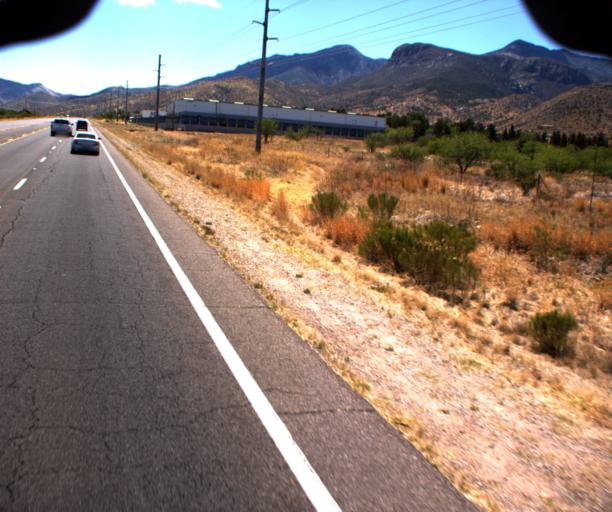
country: US
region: Arizona
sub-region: Cochise County
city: Sierra Vista Southeast
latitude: 31.4639
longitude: -110.2575
